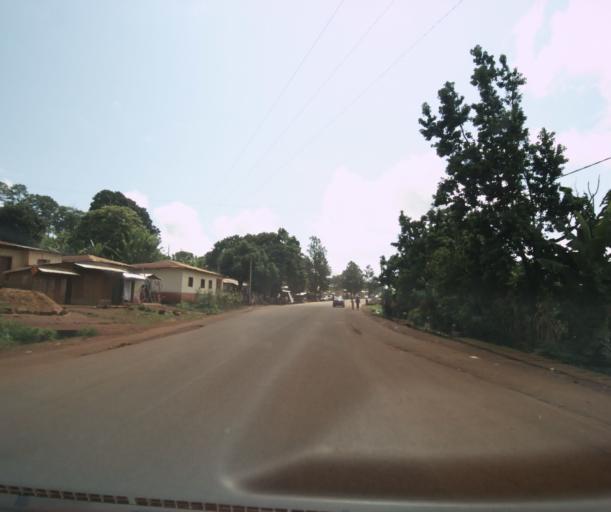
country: CM
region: West
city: Foumban
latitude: 5.7309
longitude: 10.8737
